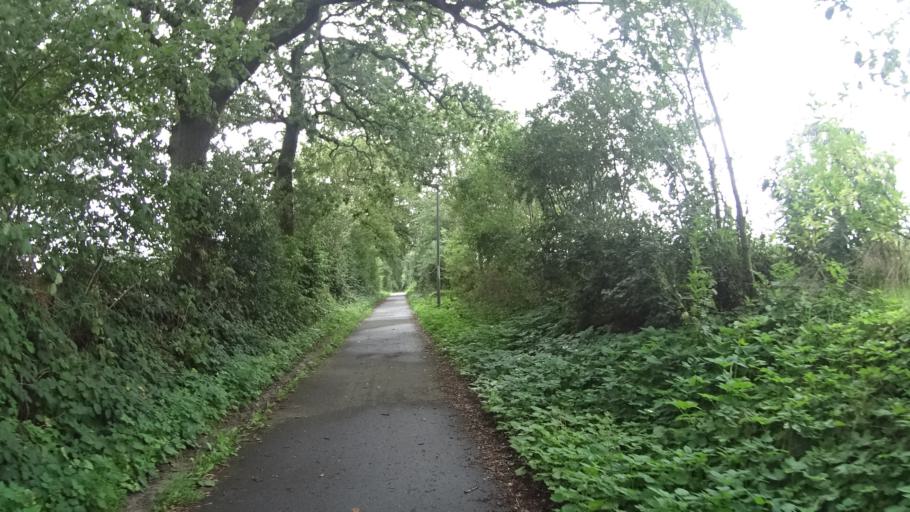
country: DE
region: Schleswig-Holstein
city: Tangstedt
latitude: 53.7398
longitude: 10.0719
